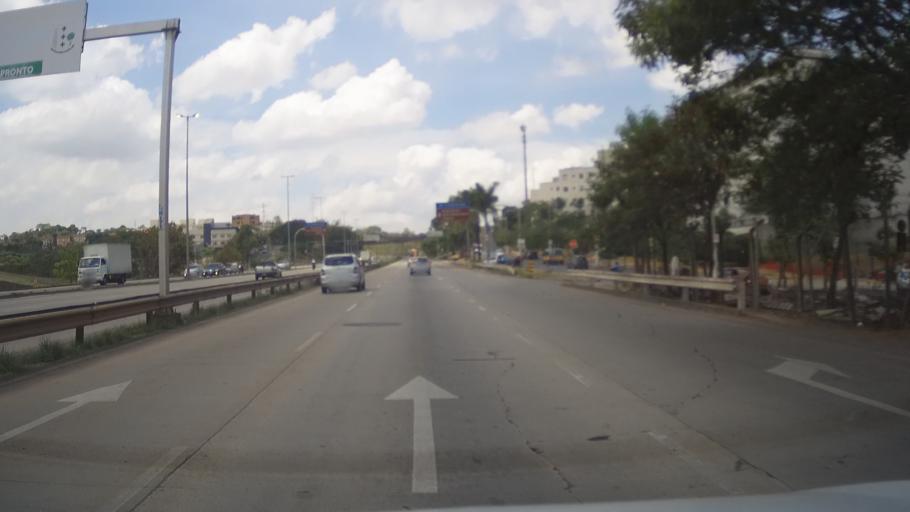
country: BR
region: Minas Gerais
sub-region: Contagem
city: Contagem
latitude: -19.9341
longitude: -44.0219
